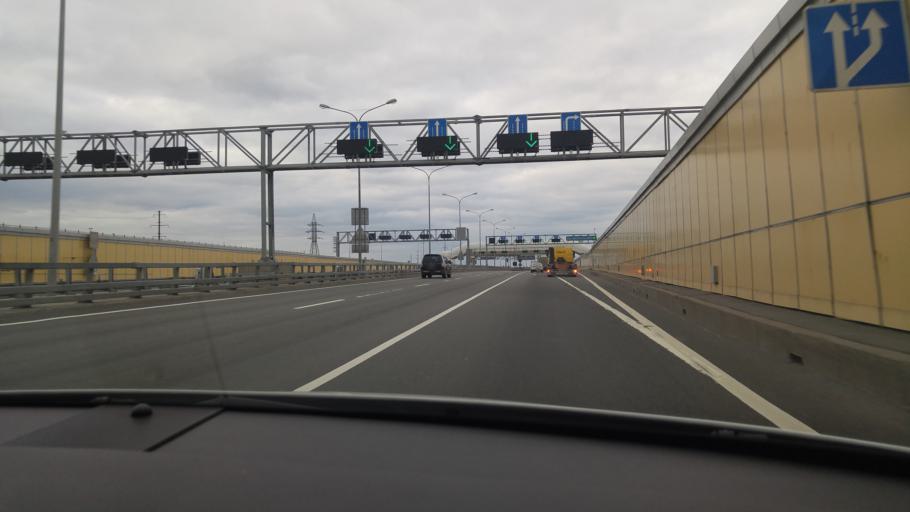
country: RU
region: St.-Petersburg
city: Kronshtadt
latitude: 59.9974
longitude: 29.7004
